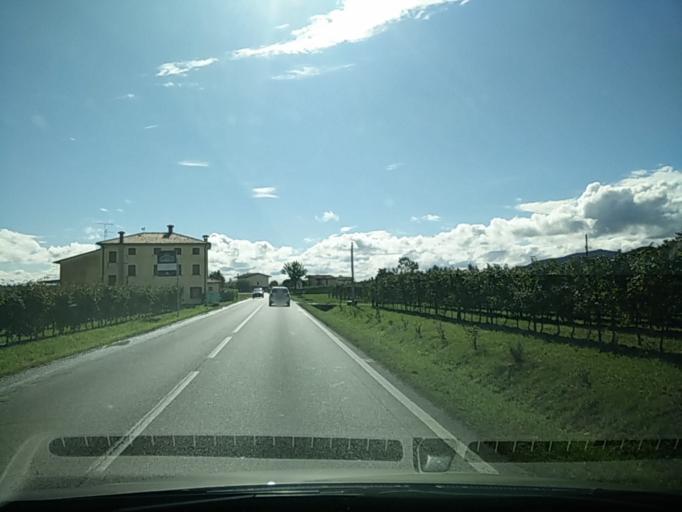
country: IT
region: Veneto
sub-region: Provincia di Treviso
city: Bigolino
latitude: 45.8755
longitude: 12.0036
